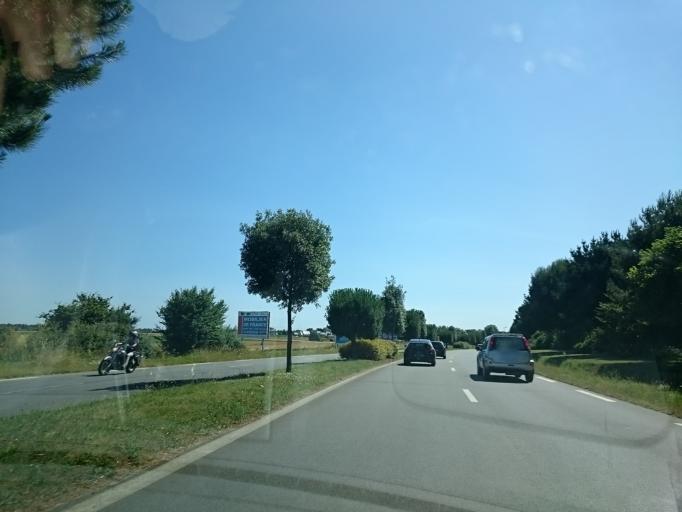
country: FR
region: Brittany
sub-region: Departement d'Ille-et-Vilaine
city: Saint-Malo
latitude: 48.6541
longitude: -1.9680
